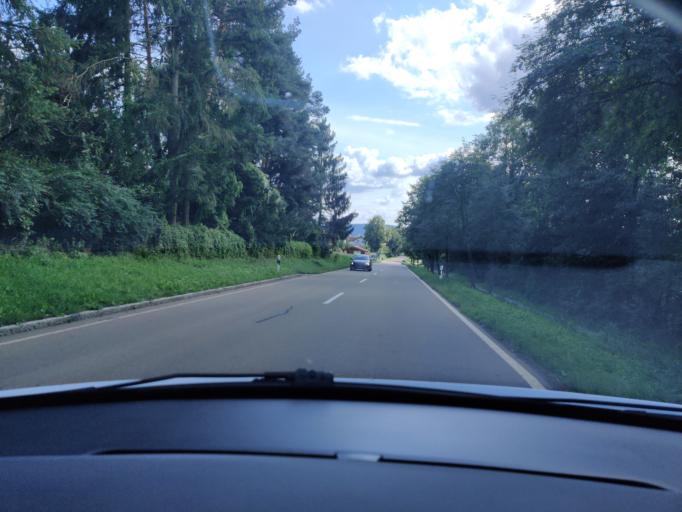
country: DE
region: Bavaria
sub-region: Upper Palatinate
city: Nabburg
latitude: 49.4660
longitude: 12.1867
